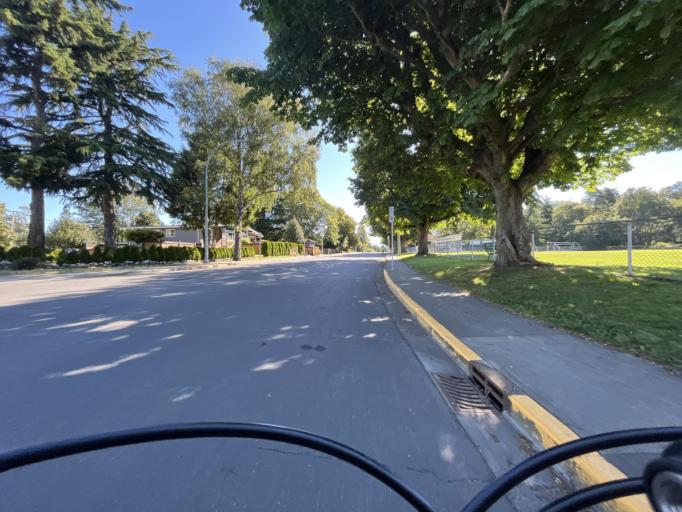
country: CA
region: British Columbia
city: Oak Bay
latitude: 48.4191
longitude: -123.3290
